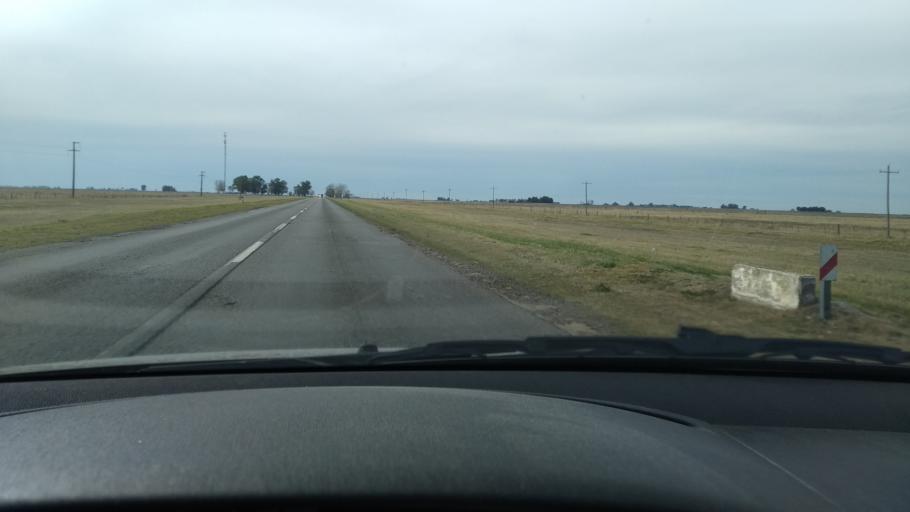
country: AR
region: Buenos Aires
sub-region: Partido de Azul
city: Azul
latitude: -36.7388
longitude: -59.7890
